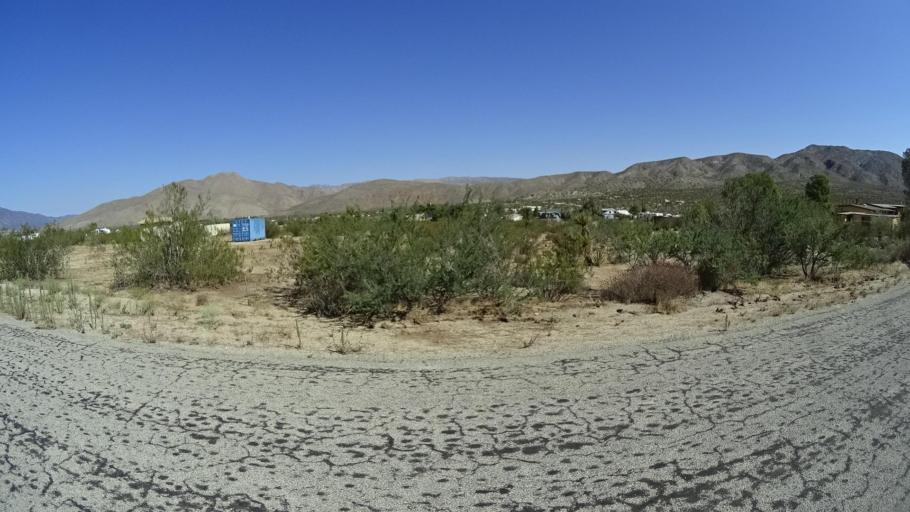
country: US
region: California
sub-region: San Diego County
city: Julian
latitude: 33.0749
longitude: -116.4391
